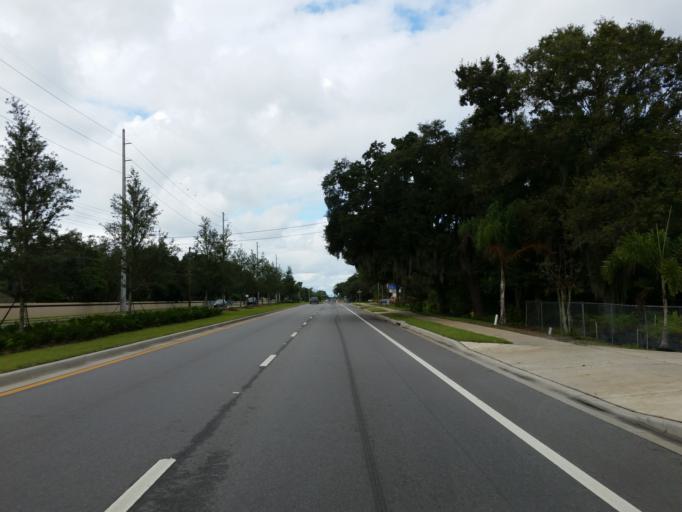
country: US
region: Florida
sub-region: Hillsborough County
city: Riverview
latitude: 27.8536
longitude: -82.2936
